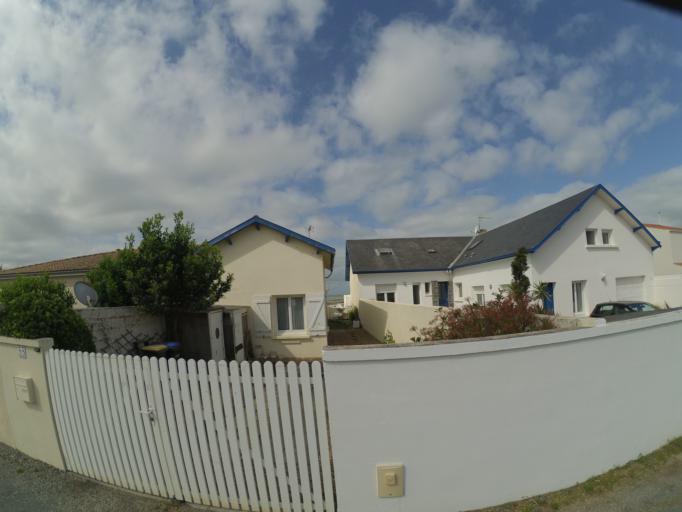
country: FR
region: Poitou-Charentes
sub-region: Departement de la Charente-Maritime
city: Angoulins
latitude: 46.1018
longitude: -1.1124
